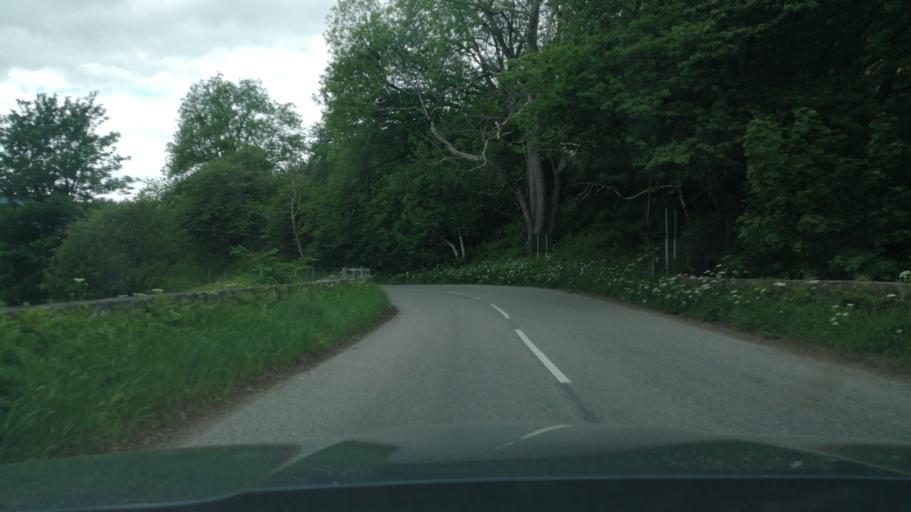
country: GB
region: Scotland
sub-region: Moray
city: Rothes
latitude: 57.5575
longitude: -3.1524
